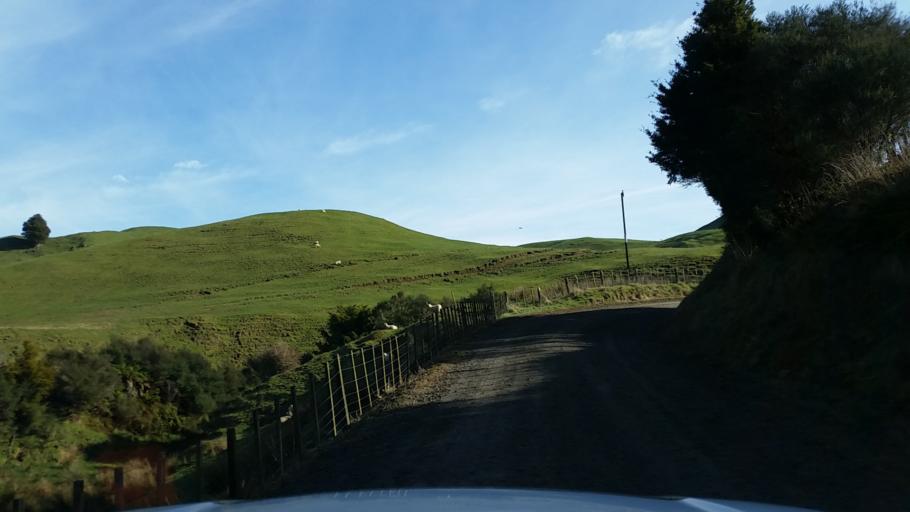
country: NZ
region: Taranaki
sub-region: South Taranaki District
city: Eltham
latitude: -39.3162
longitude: 174.5339
